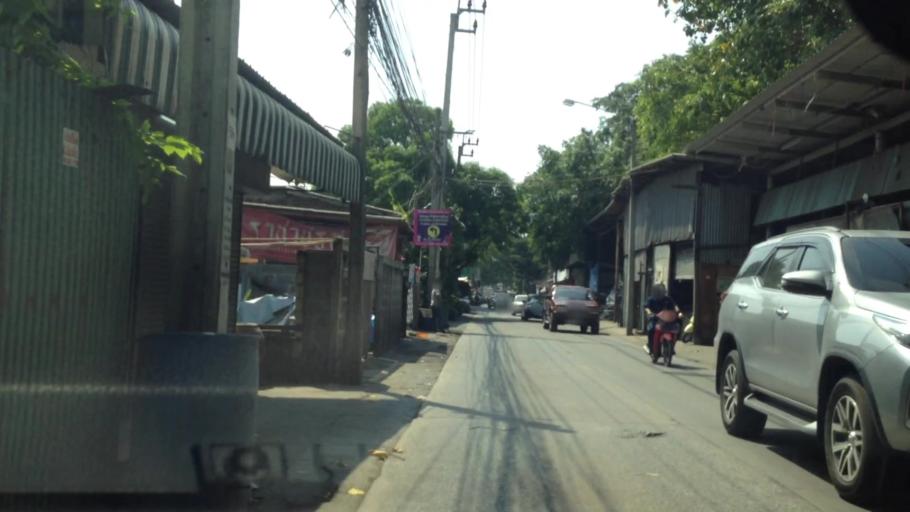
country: TH
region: Bangkok
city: Sai Mai
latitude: 13.9089
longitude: 100.6263
